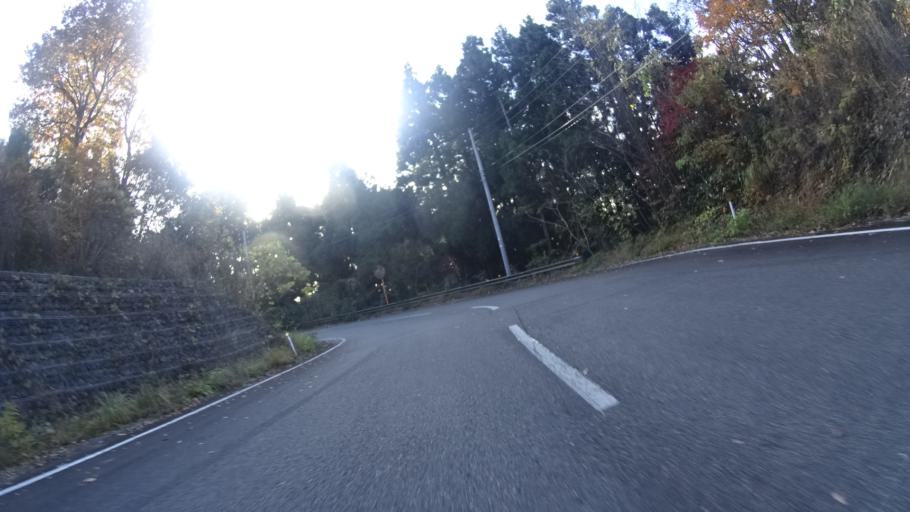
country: JP
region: Niigata
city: Yoshida-kasugacho
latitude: 37.6622
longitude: 138.8131
